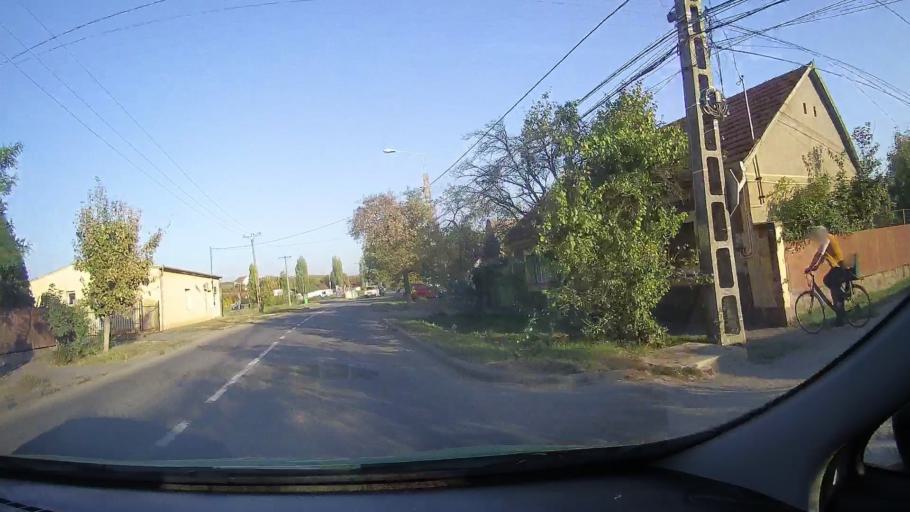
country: RO
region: Bihor
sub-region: Comuna Biharea
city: Biharea
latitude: 47.1035
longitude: 21.8915
